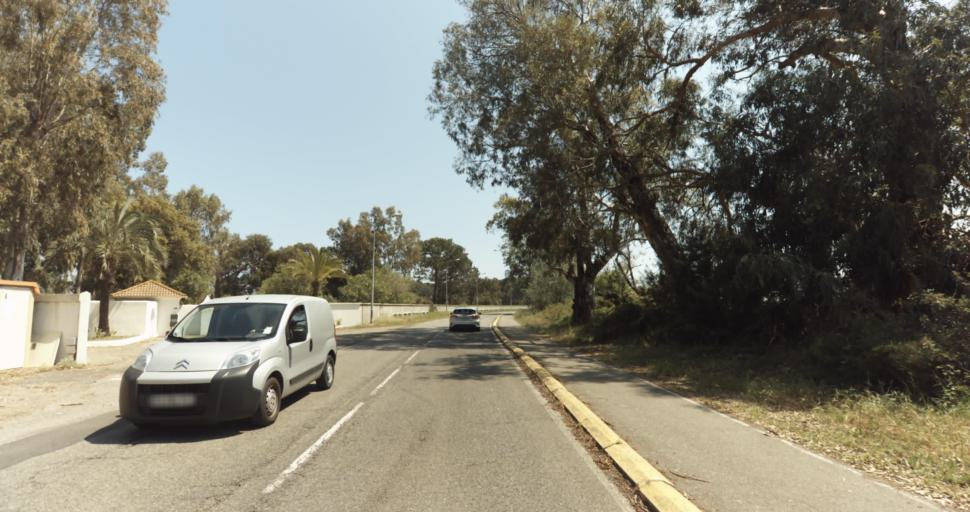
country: FR
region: Corsica
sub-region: Departement de la Haute-Corse
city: Biguglia
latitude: 42.6228
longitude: 9.4724
